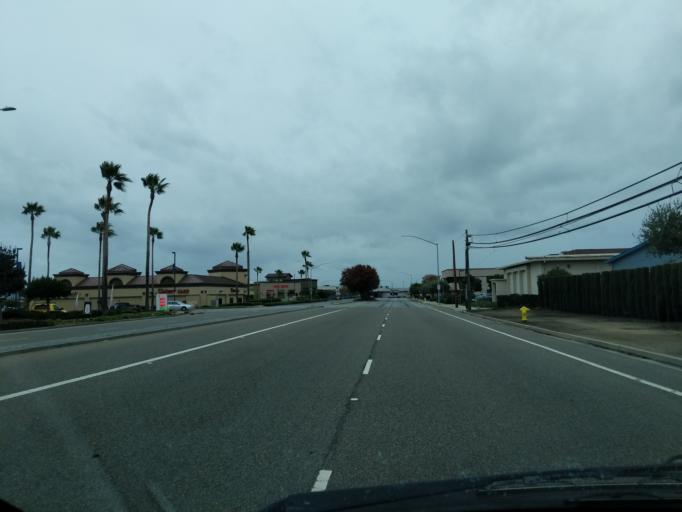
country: US
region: California
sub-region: Monterey County
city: Boronda
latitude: 36.7188
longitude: -121.6527
